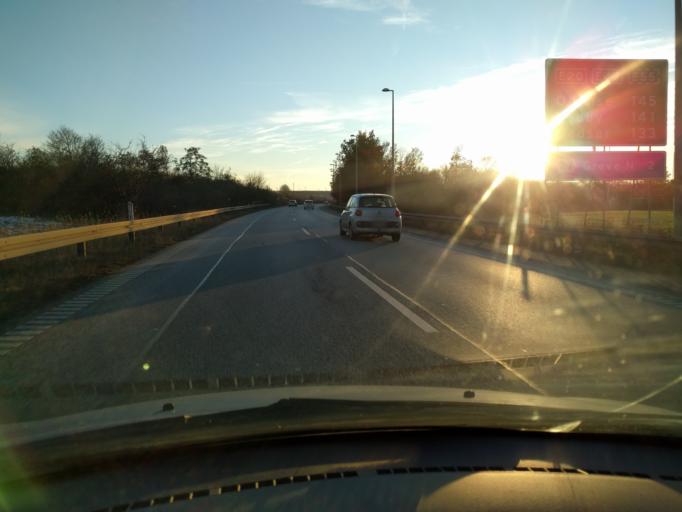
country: DK
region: Capital Region
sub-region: Ishoj Kommune
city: Ishoj
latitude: 55.6158
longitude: 12.3259
